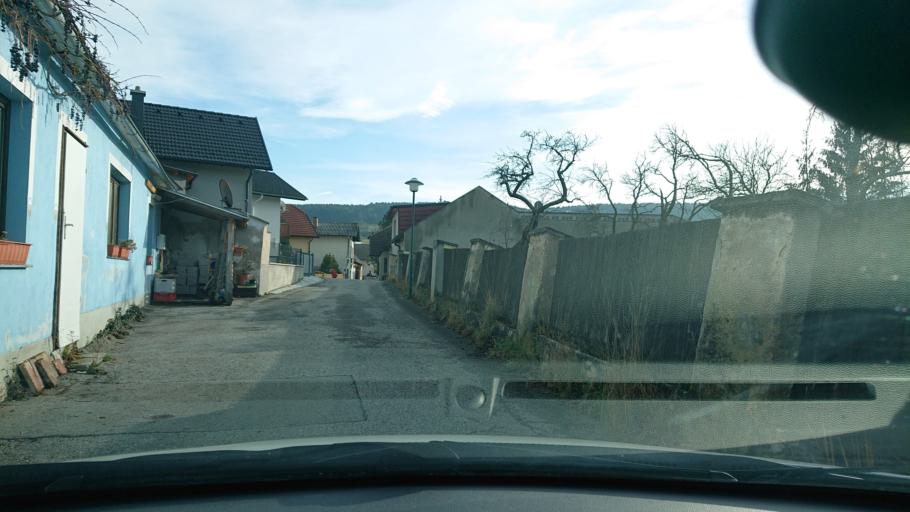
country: AT
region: Lower Austria
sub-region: Politischer Bezirk Baden
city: Hernstein
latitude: 47.8955
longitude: 16.1050
